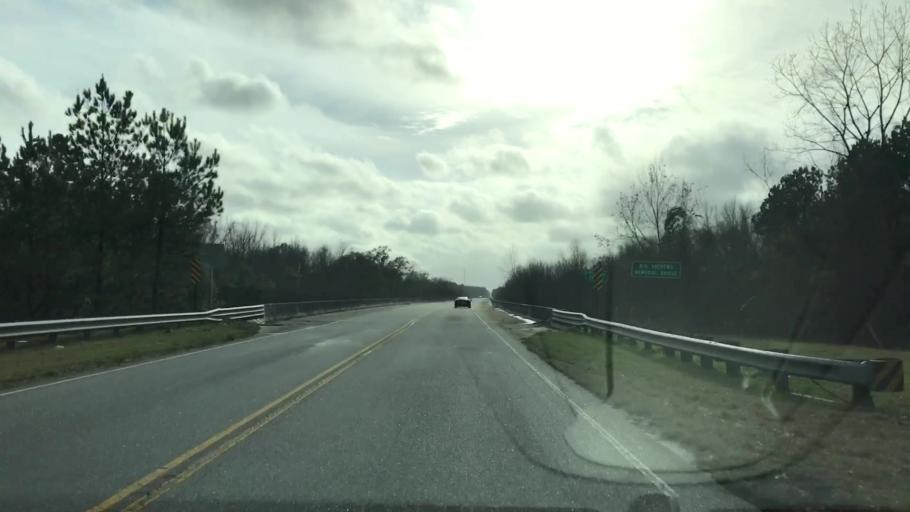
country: US
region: South Carolina
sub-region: Williamsburg County
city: Andrews
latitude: 33.3111
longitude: -79.6728
